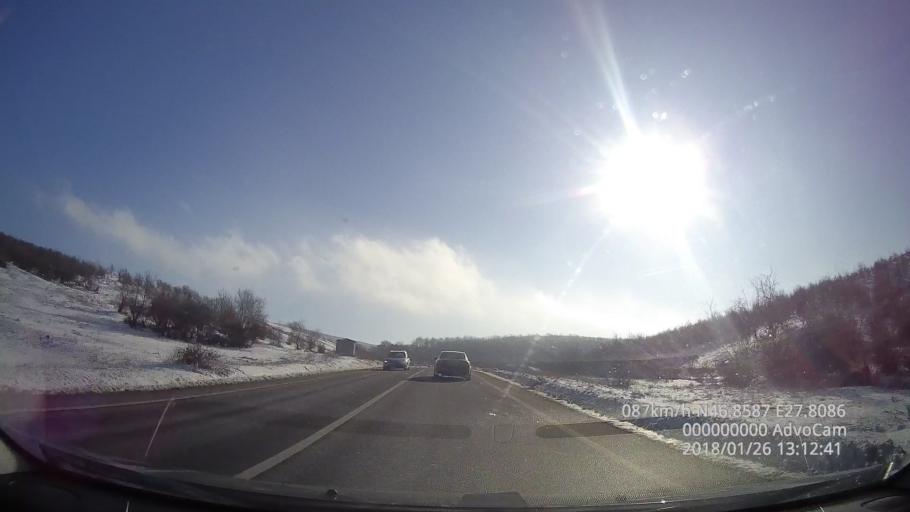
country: RO
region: Vaslui
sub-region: Comuna Miclesti
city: Chircesti
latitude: 46.8582
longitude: 27.8093
